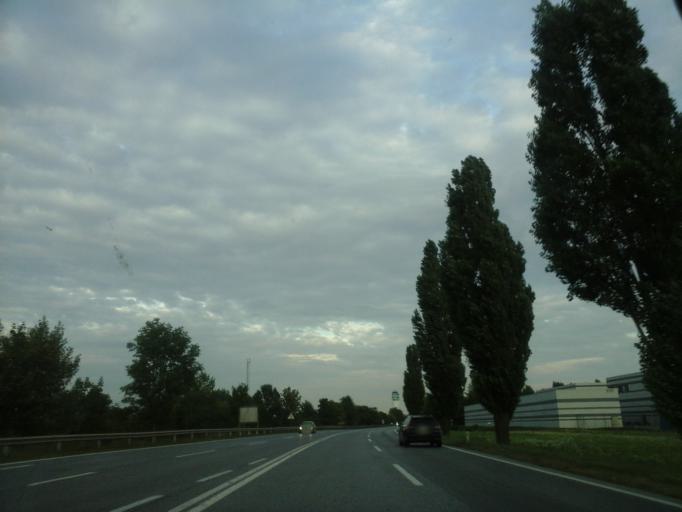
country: AT
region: Lower Austria
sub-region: Politischer Bezirk Wien-Umgebung
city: Rauchenwarth
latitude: 48.1320
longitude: 16.5366
